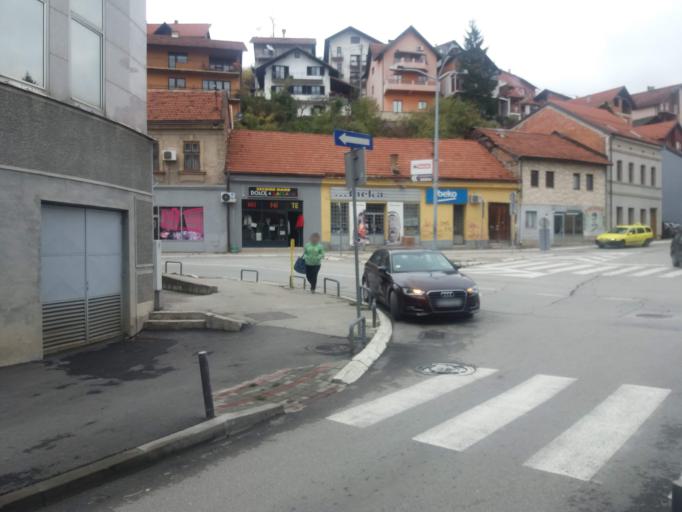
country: RS
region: Central Serbia
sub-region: Zlatiborski Okrug
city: Uzice
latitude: 43.8575
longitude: 19.8463
